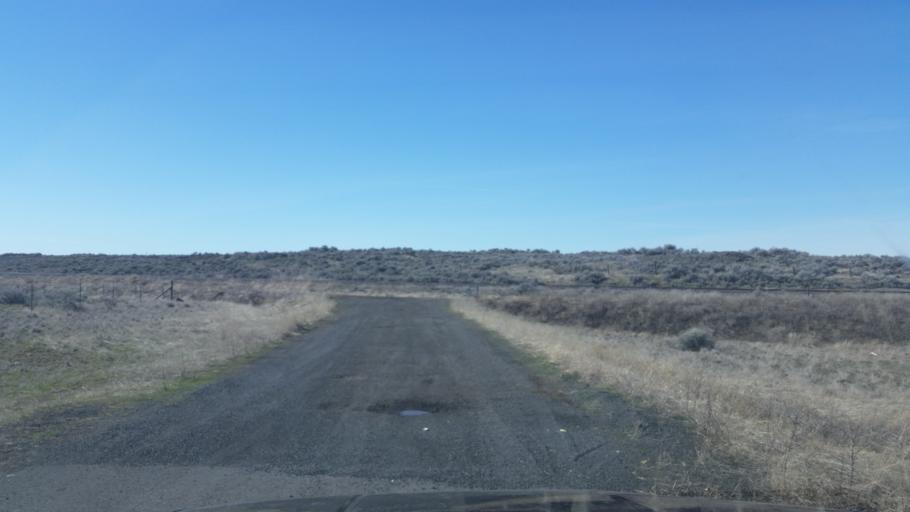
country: US
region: Washington
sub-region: Lincoln County
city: Davenport
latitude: 47.6532
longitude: -118.3356
